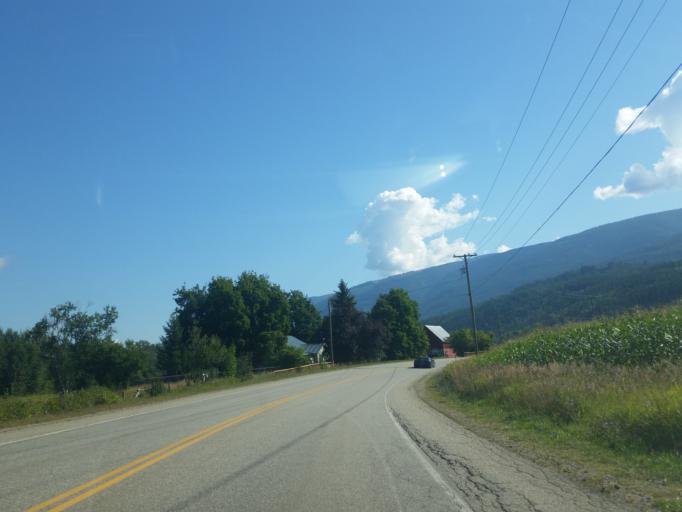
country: CA
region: British Columbia
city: Enderby
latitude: 50.6448
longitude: -119.1002
